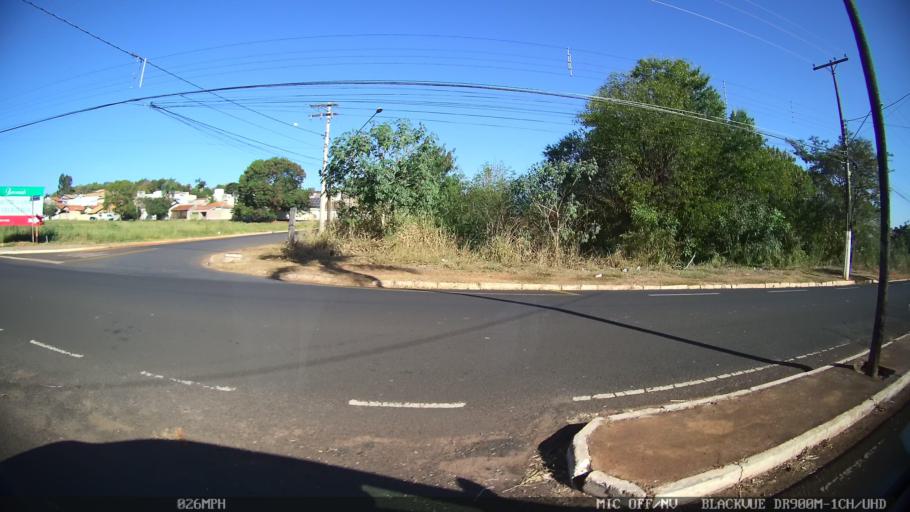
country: BR
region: Sao Paulo
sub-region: Olimpia
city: Olimpia
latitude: -20.7435
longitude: -48.9019
